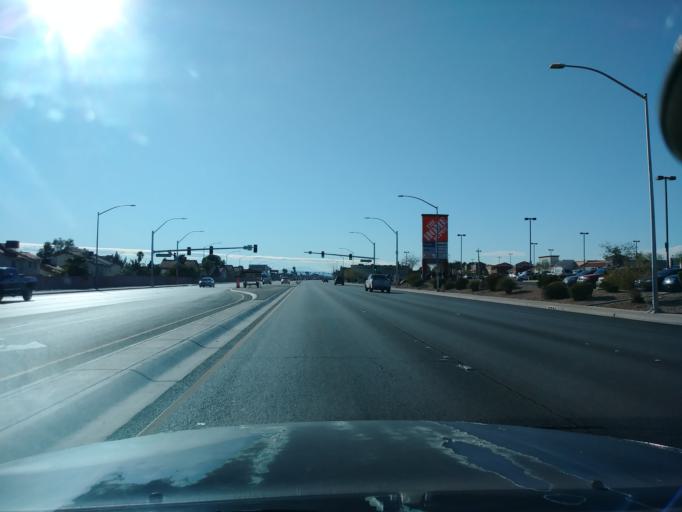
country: US
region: Nevada
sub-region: Clark County
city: Spring Valley
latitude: 36.1638
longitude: -115.2442
